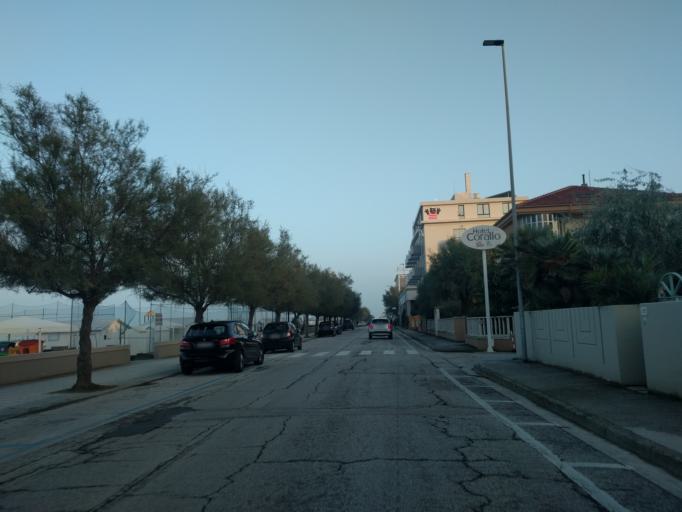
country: IT
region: The Marches
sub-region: Provincia di Ancona
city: Senigallia
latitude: 43.7243
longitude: 13.2110
